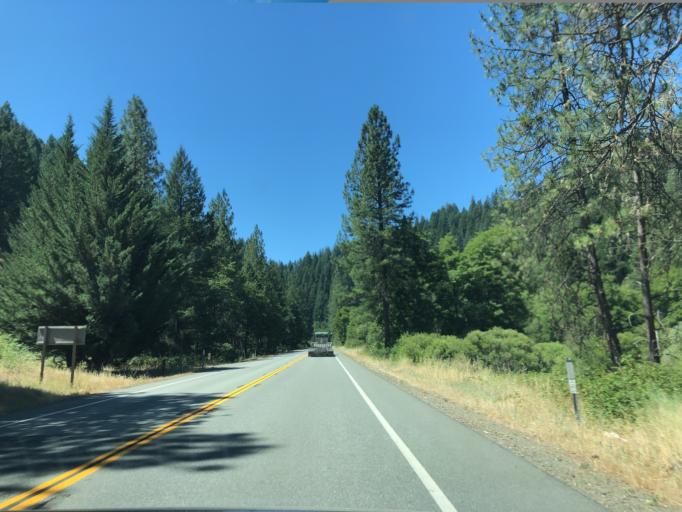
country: US
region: California
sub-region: Trinity County
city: Weaverville
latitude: 40.6938
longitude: -122.9302
